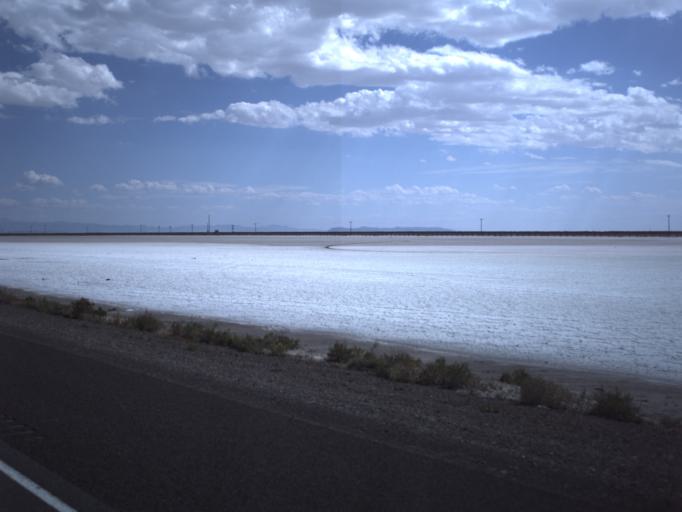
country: US
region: Utah
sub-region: Tooele County
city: Wendover
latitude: 40.7352
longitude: -113.6928
